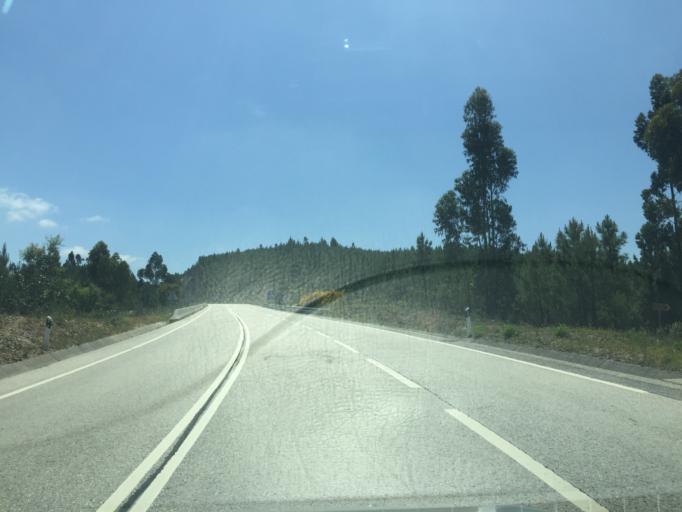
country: PT
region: Castelo Branco
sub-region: Vila de Rei
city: Vila de Rei
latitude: 39.7126
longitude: -8.1418
